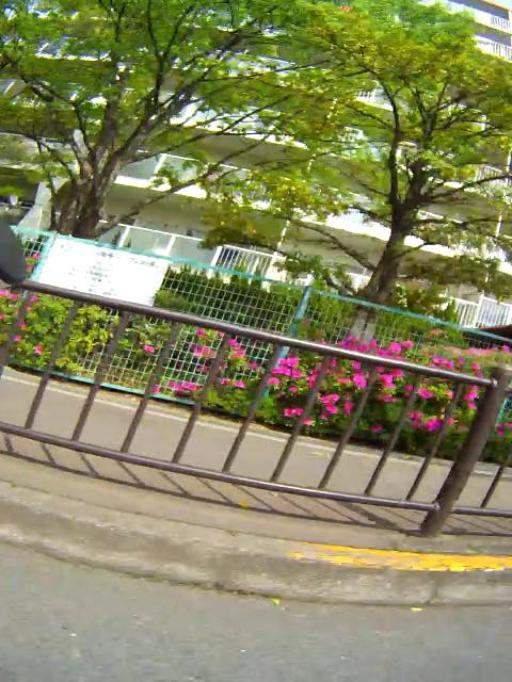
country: JP
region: Osaka
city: Mino
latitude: 34.8132
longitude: 135.4743
